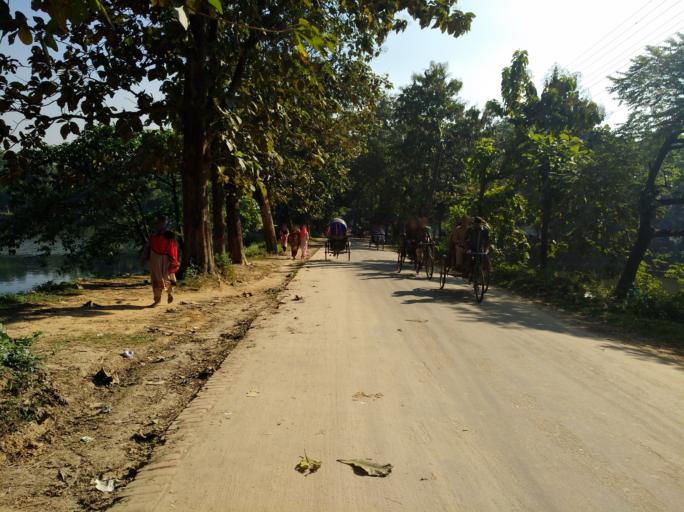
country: BD
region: Dhaka
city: Tungi
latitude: 23.8864
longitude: 90.2663
